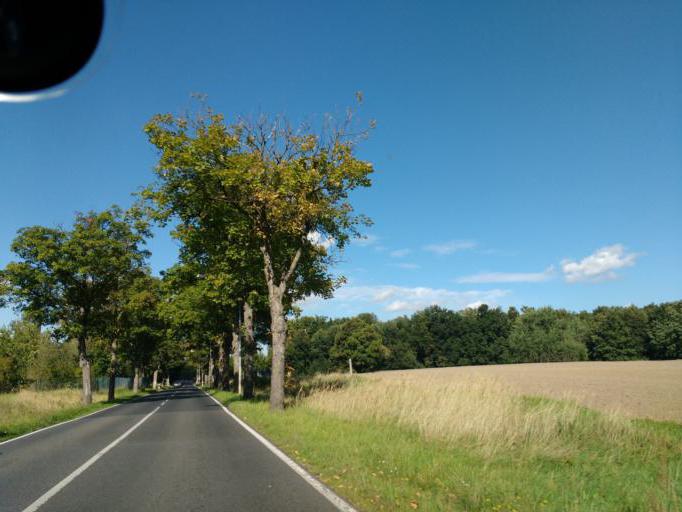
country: DE
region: Brandenburg
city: Mittenwalde
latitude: 52.2458
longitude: 13.5681
